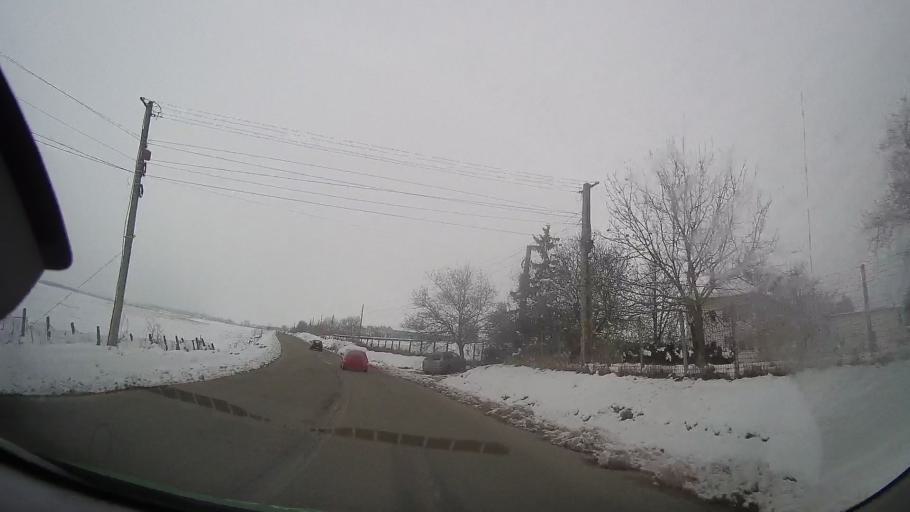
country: RO
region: Vaslui
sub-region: Comuna Negresti
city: Negresti
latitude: 46.8370
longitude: 27.4425
